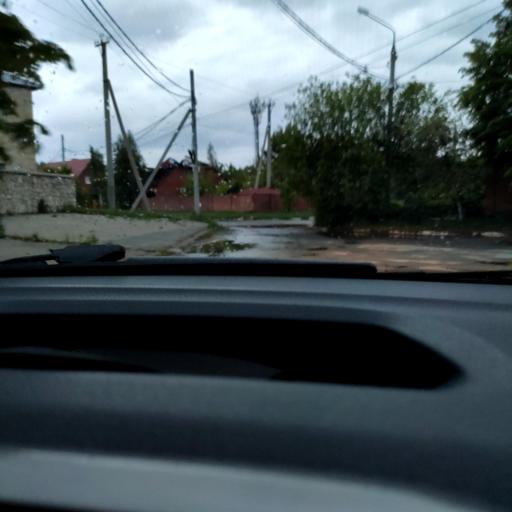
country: RU
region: Samara
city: Tol'yatti
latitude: 53.5419
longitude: 49.3747
